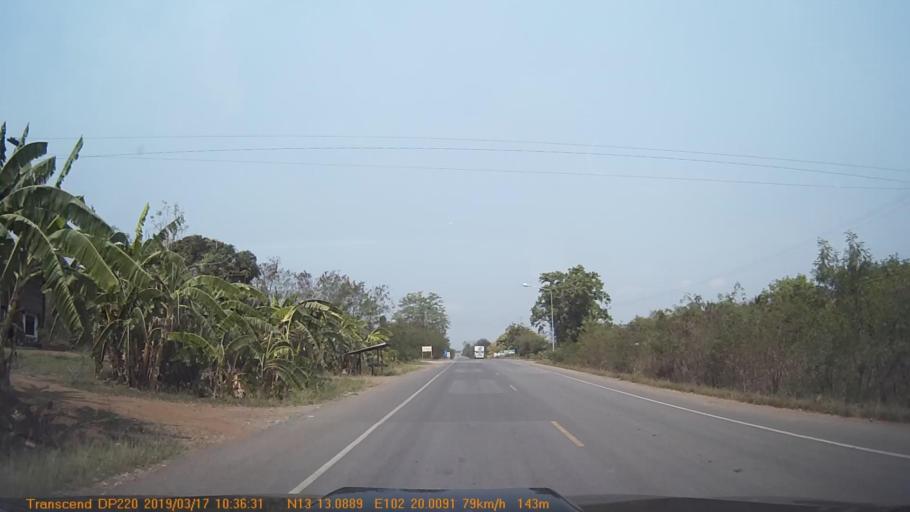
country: TH
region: Chanthaburi
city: Soi Dao
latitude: 13.2183
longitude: 102.3331
